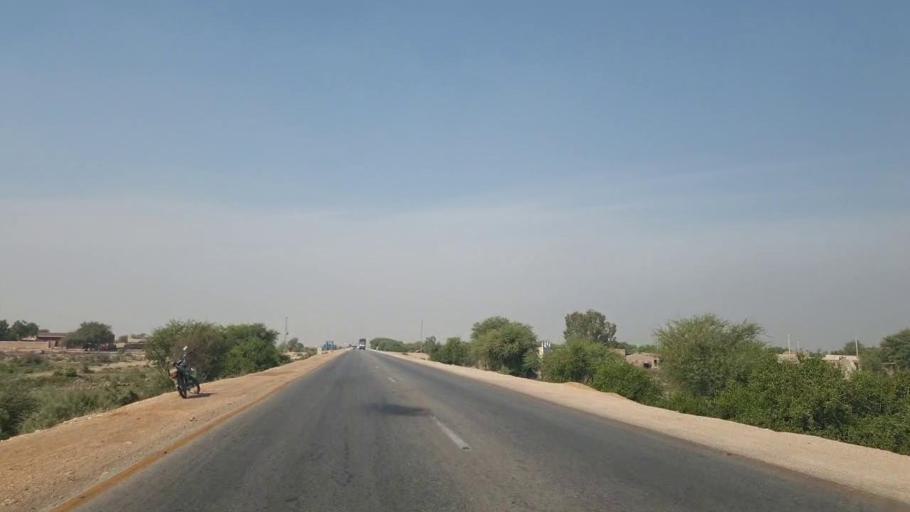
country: PK
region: Sindh
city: Hala
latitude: 25.8749
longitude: 68.2521
